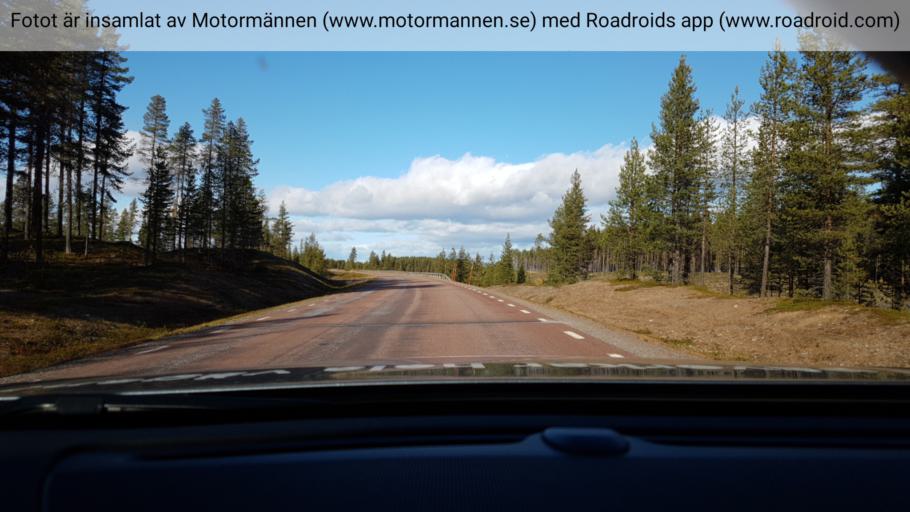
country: SE
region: Norrbotten
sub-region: Arjeplogs Kommun
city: Arjeplog
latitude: 66.0335
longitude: 18.0562
